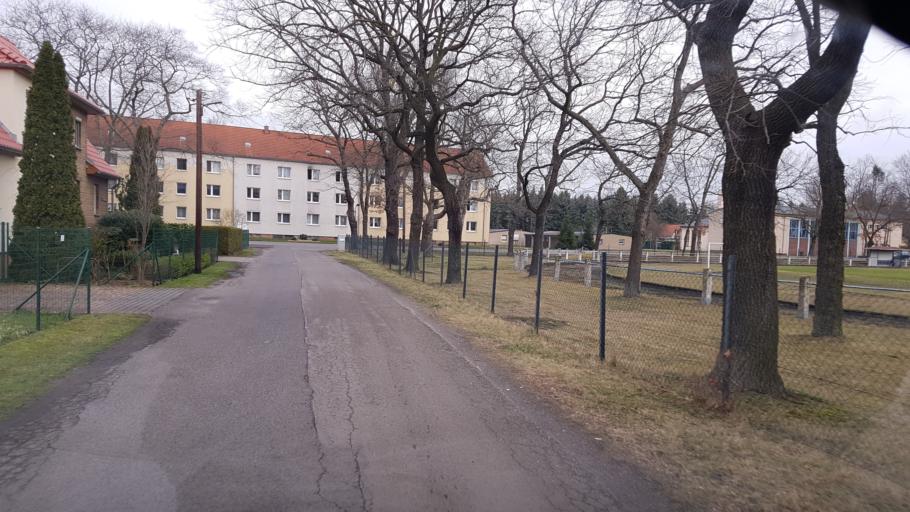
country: DE
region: Brandenburg
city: Ruhland
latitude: 51.4551
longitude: 13.8550
